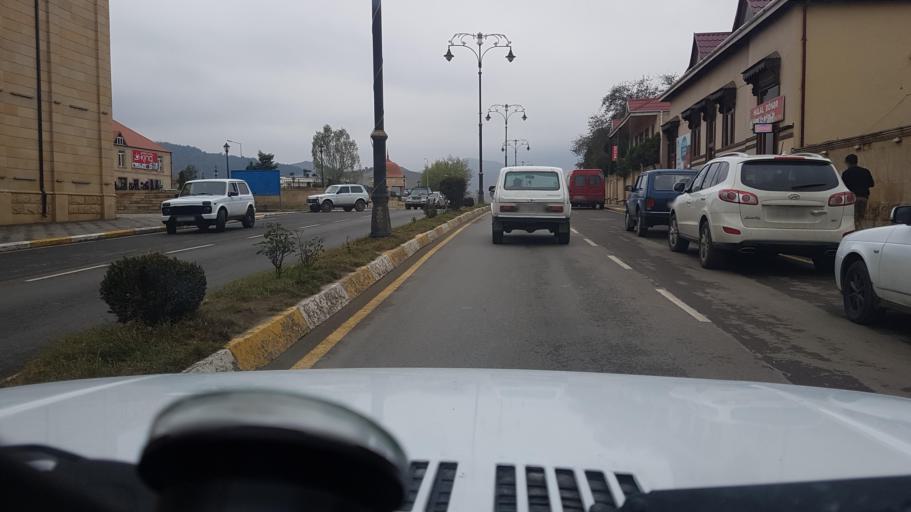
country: AZ
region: Gadabay Rayon
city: Kyadabek
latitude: 40.5763
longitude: 45.8084
